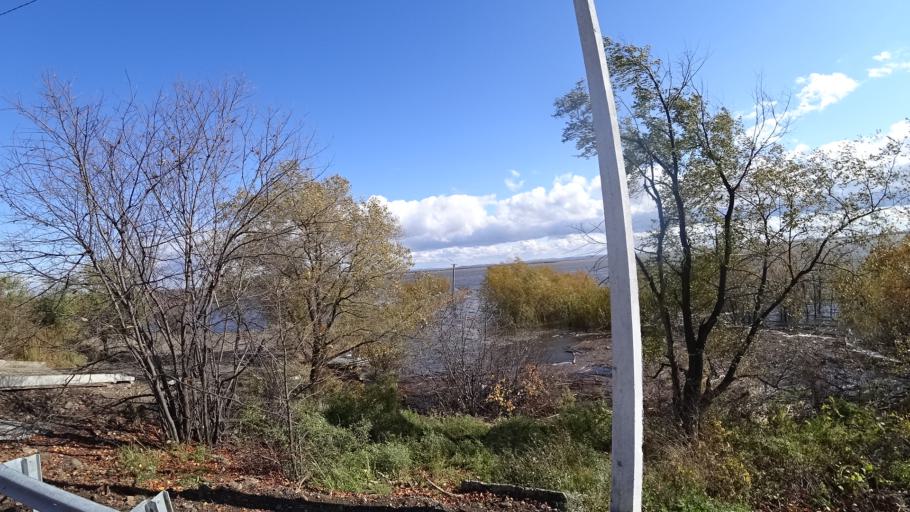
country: RU
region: Khabarovsk Krai
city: Amursk
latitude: 50.2160
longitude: 136.9074
